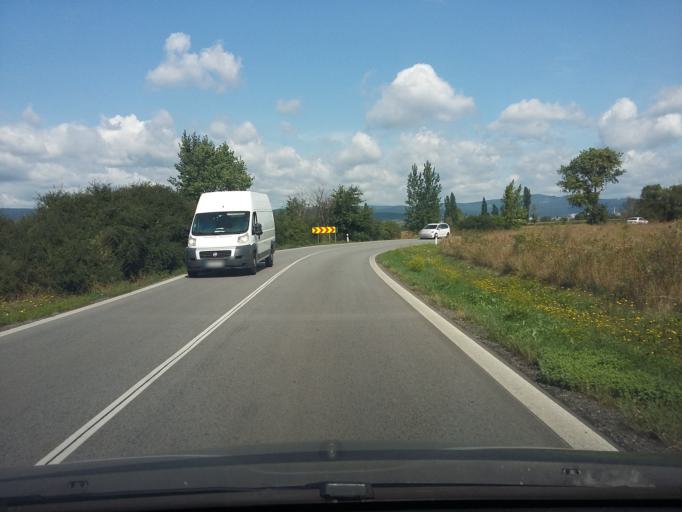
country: SK
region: Bratislavsky
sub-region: Okres Pezinok
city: Pezinok
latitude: 48.2534
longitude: 17.2610
